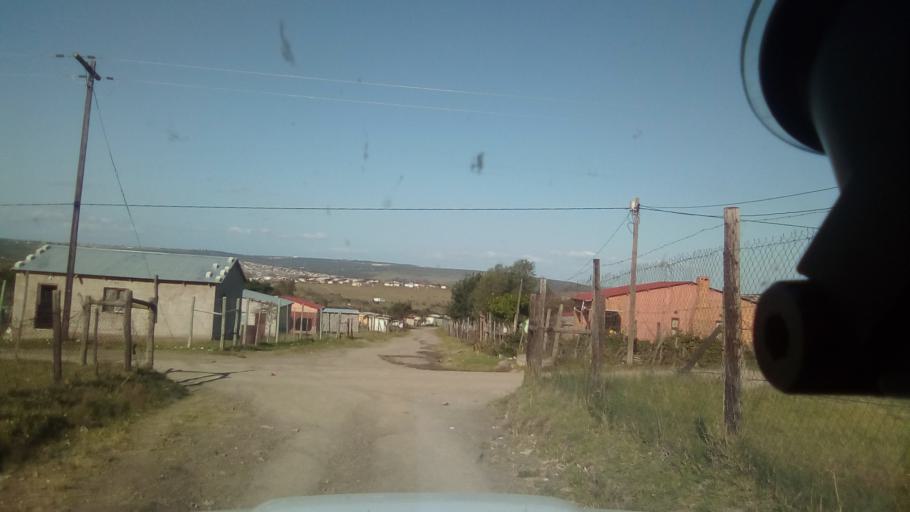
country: ZA
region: Eastern Cape
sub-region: Buffalo City Metropolitan Municipality
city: Bhisho
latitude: -32.8113
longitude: 27.3574
